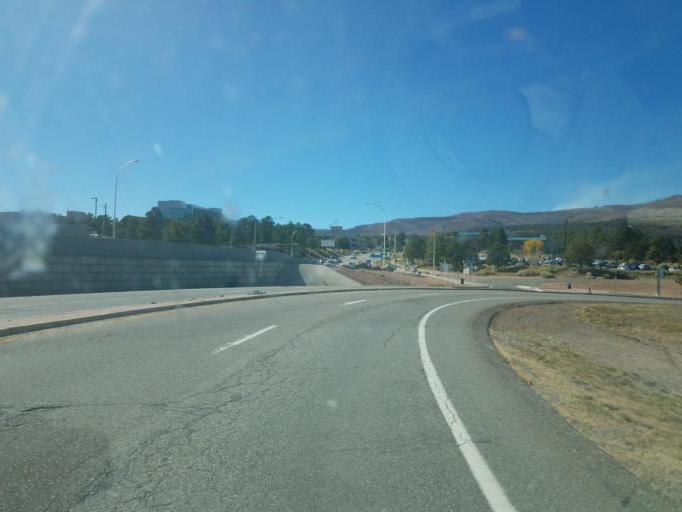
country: US
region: New Mexico
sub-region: Los Alamos County
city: Los Alamos
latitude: 35.8781
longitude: -106.3208
